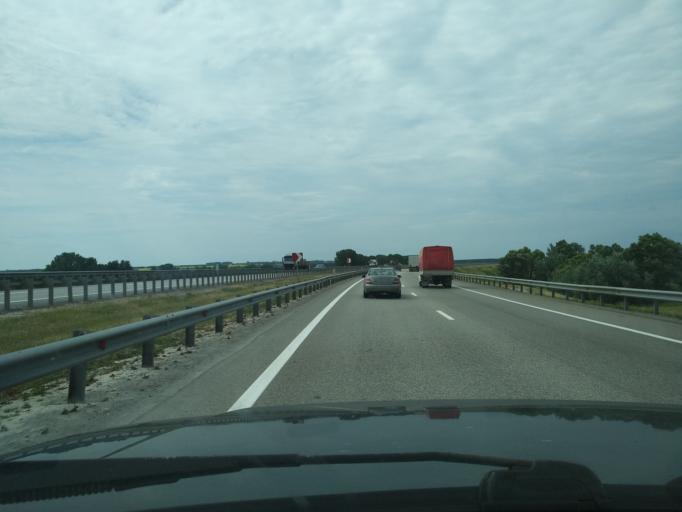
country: RU
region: Lipetsk
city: Khlevnoye
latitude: 52.0606
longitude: 39.1831
